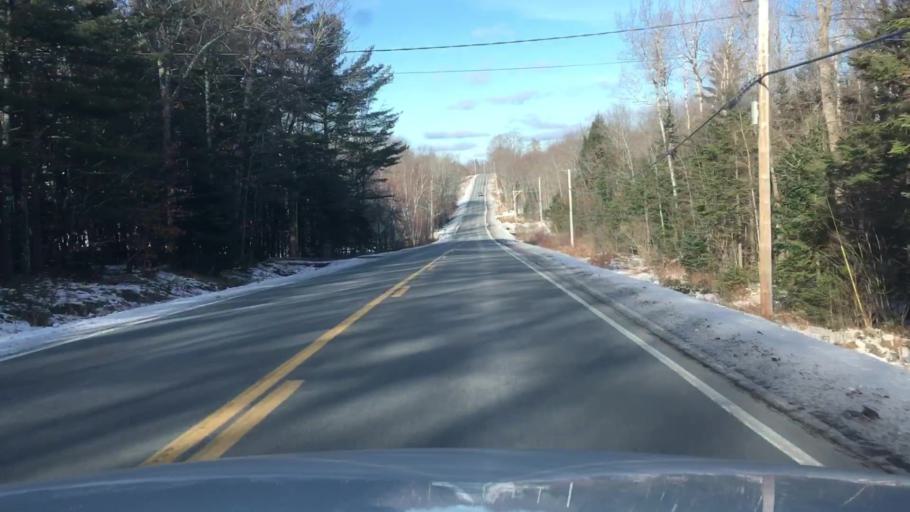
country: US
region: Maine
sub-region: Penobscot County
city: Holden
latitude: 44.7595
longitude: -68.5957
